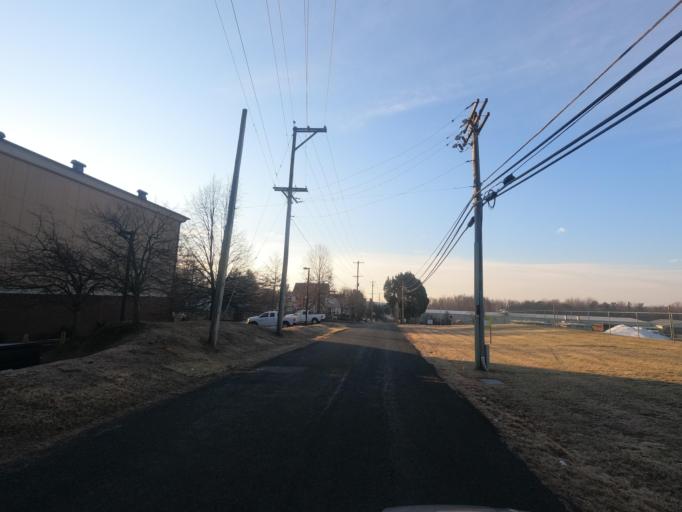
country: US
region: Maryland
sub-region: Cecil County
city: North East
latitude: 39.6206
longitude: -75.9521
